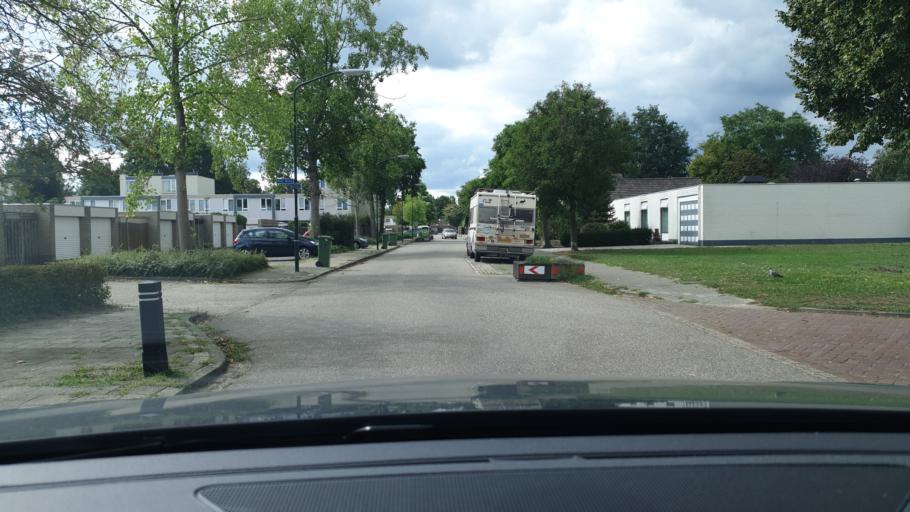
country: NL
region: North Brabant
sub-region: Gemeente Veghel
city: Veghel
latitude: 51.6095
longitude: 5.5391
